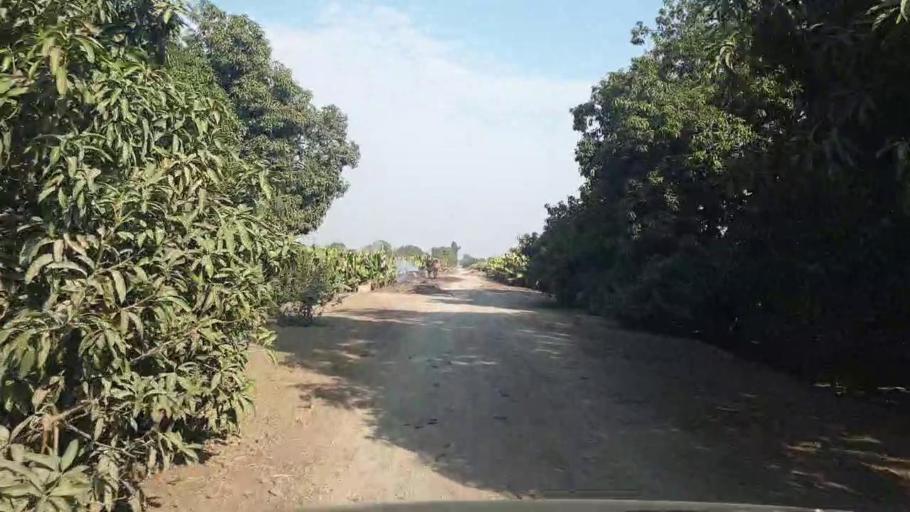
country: PK
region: Sindh
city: Tando Adam
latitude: 25.7561
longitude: 68.5883
